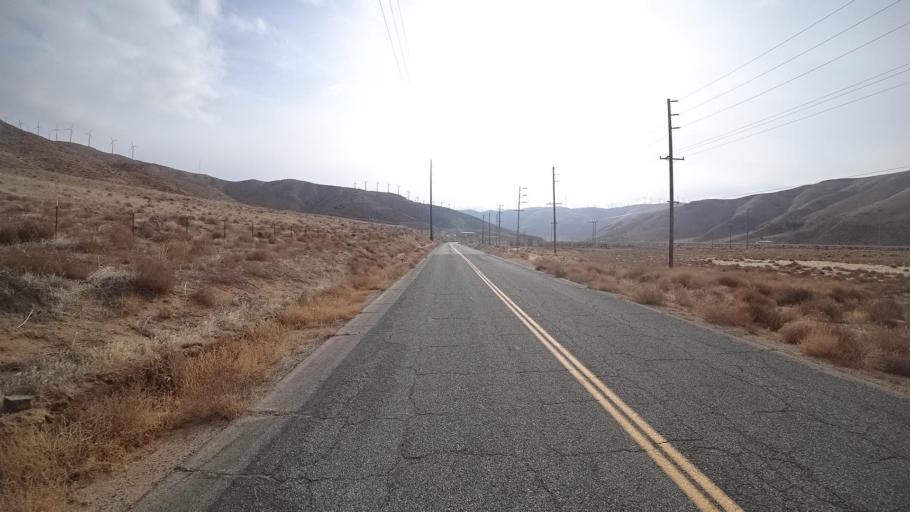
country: US
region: California
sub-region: Kern County
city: Tehachapi
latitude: 35.1091
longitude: -118.3150
